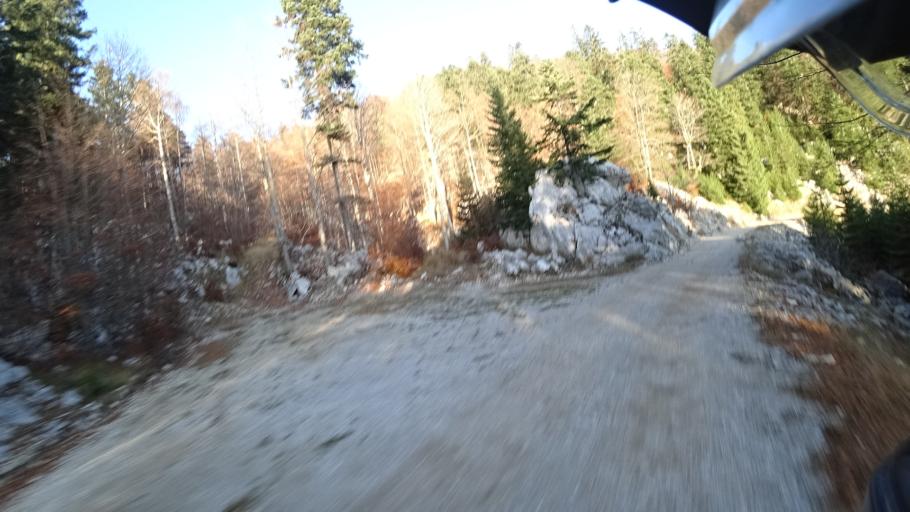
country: HR
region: Primorsko-Goranska
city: Drazice
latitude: 45.4918
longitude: 14.4855
